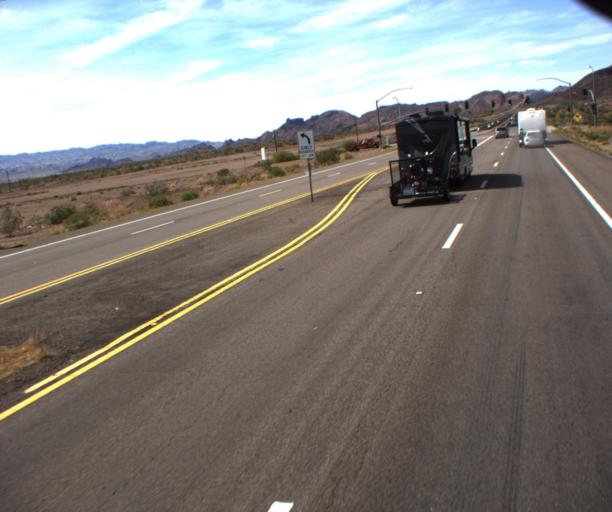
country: US
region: Arizona
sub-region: Mohave County
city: Desert Hills
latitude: 34.5780
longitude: -114.3664
